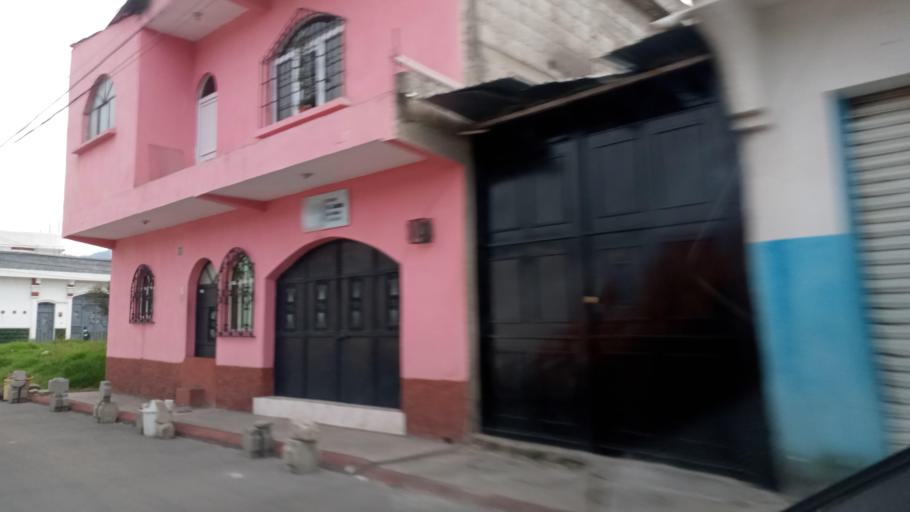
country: GT
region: Quetzaltenango
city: Quetzaltenango
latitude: 14.8422
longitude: -91.5084
